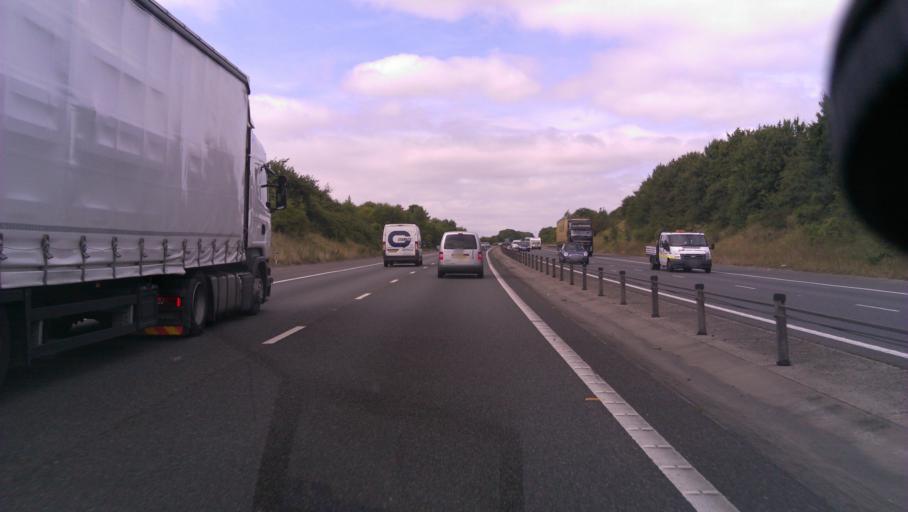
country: GB
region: England
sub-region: Essex
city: Saffron Walden
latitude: 51.9840
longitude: 0.1979
